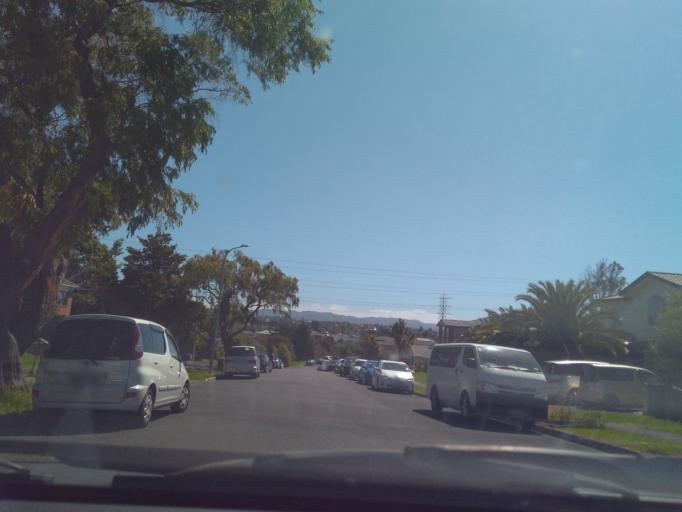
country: NZ
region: Auckland
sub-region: Auckland
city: Rosebank
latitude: -36.9009
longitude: 174.6898
